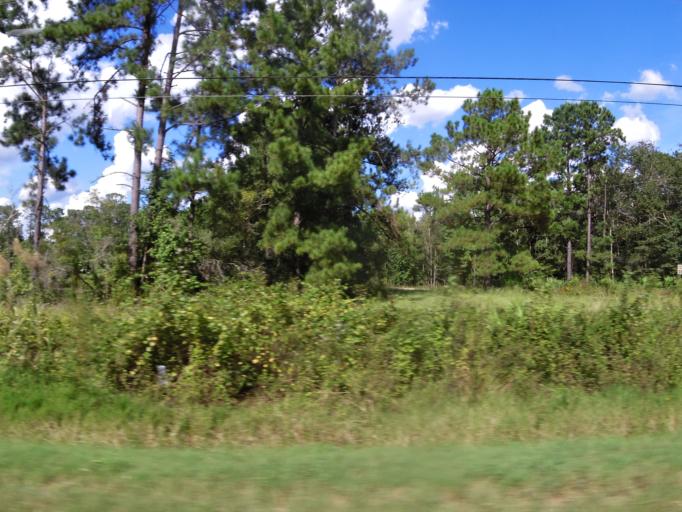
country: US
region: Georgia
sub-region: Lowndes County
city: Valdosta
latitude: 30.7879
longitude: -83.1727
